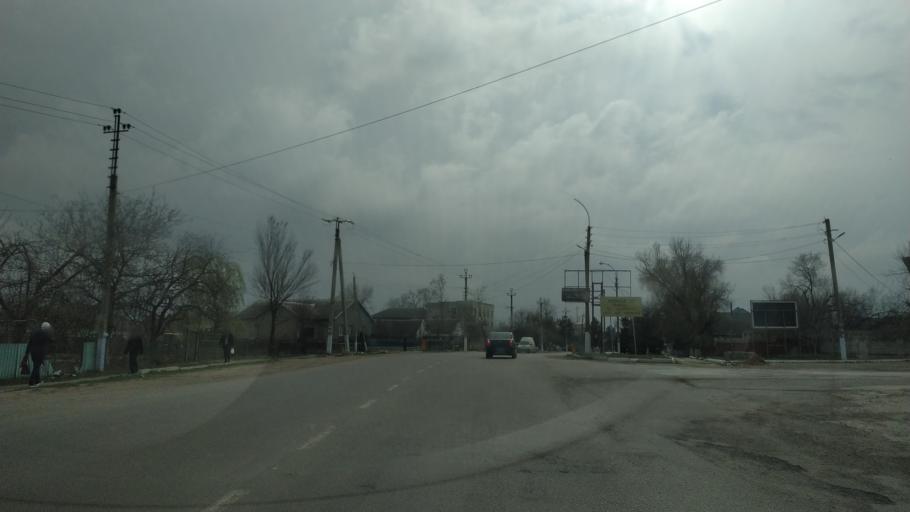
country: MD
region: Basarabeasca
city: Basarabeasca
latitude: 46.3382
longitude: 28.9566
